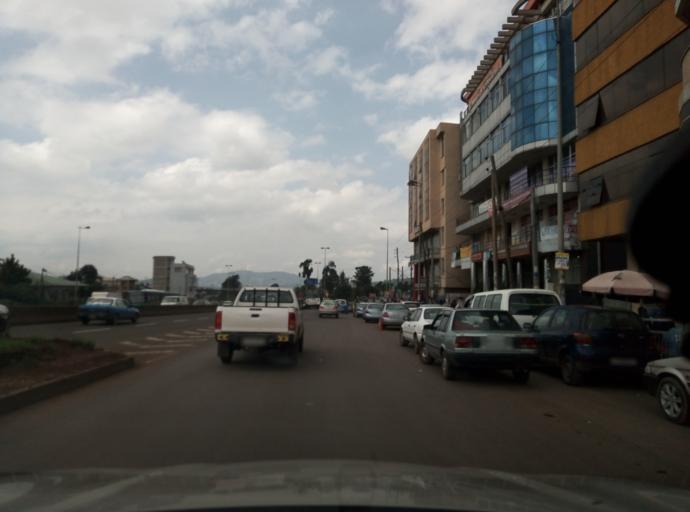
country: ET
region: Adis Abeba
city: Addis Ababa
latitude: 9.0077
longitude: 38.7193
